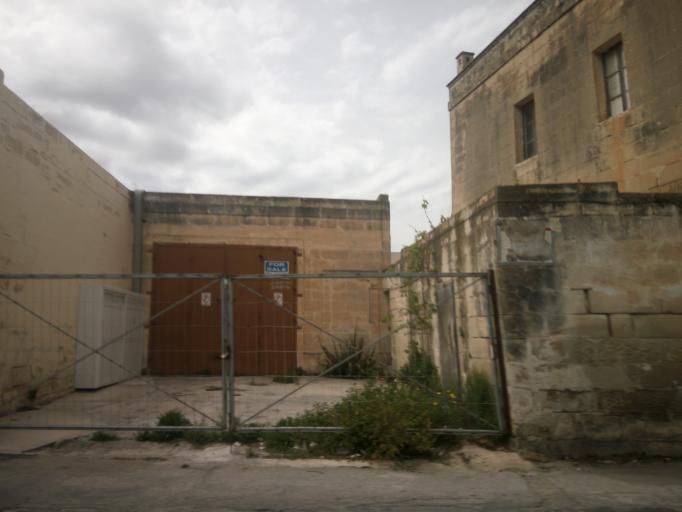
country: MT
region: Luqa
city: Luqa
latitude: 35.8643
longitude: 14.4900
